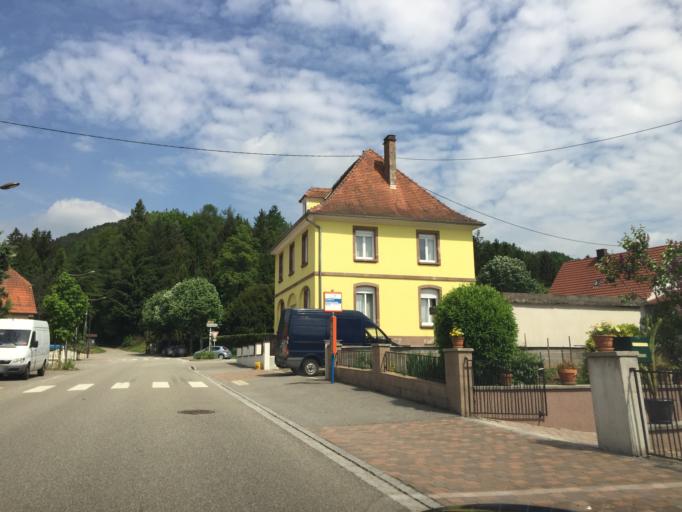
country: FR
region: Alsace
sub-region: Departement du Bas-Rhin
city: Lembach
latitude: 49.0090
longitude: 7.7889
